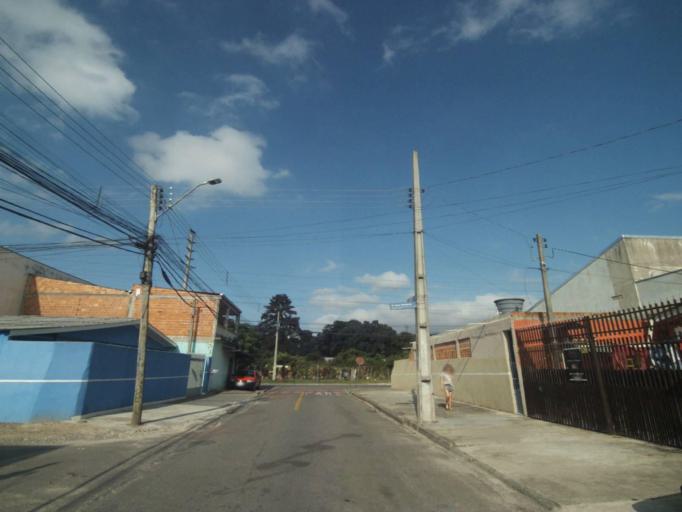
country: BR
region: Parana
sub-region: Araucaria
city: Araucaria
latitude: -25.5313
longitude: -49.3323
